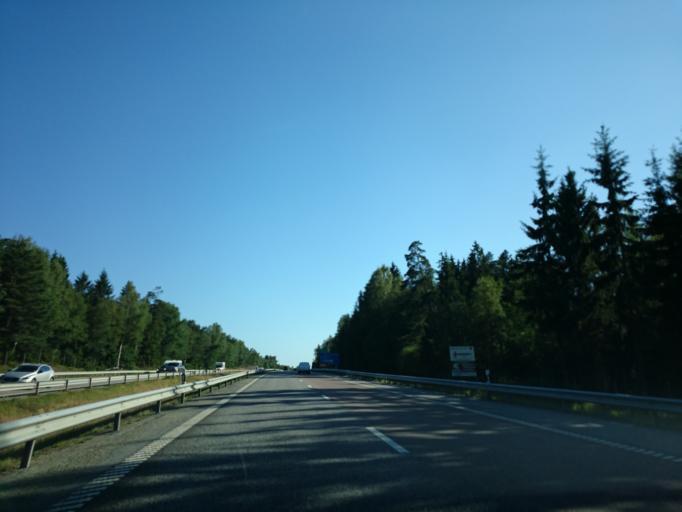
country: SE
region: Stockholm
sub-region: Sodertalje Kommun
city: Pershagen
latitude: 59.1010
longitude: 17.6076
